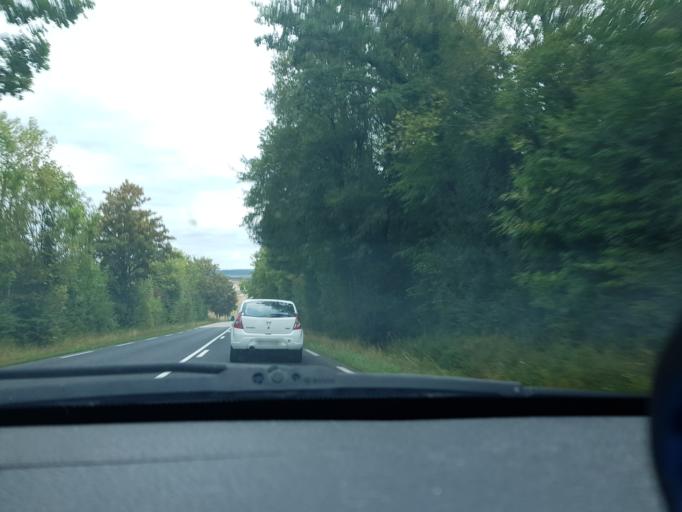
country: FR
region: Lorraine
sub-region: Departement de la Moselle
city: Chateau-Salins
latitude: 48.7718
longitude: 6.4483
